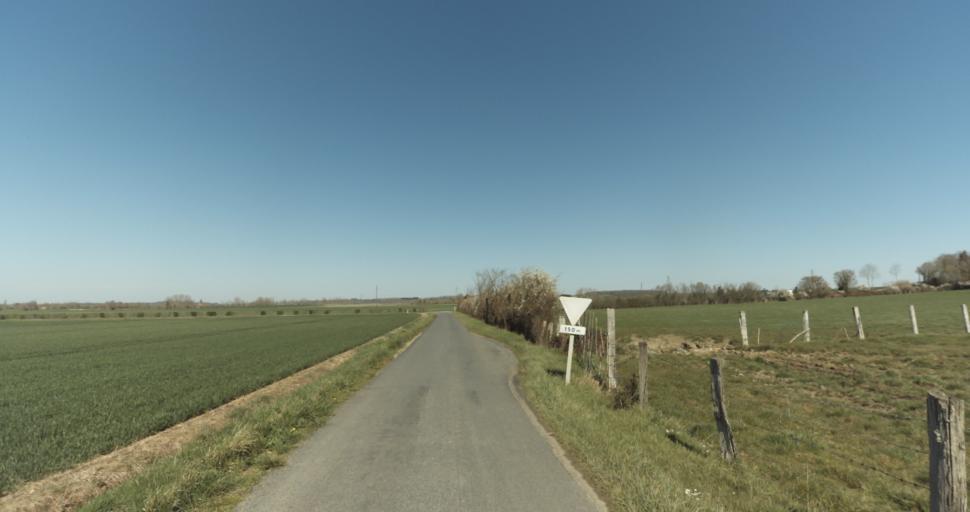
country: FR
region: Lower Normandy
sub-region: Departement du Calvados
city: Saint-Pierre-sur-Dives
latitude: 49.0168
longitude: 0.0295
